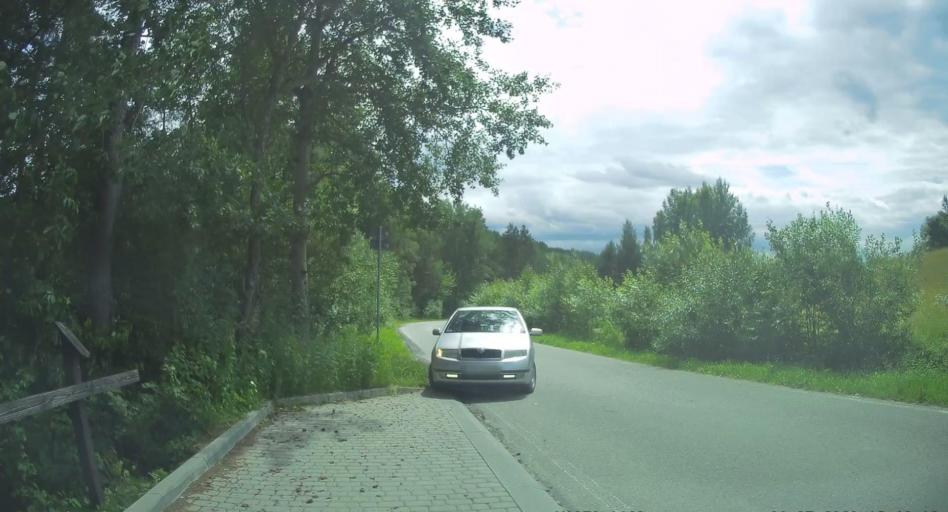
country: PL
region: Lesser Poland Voivodeship
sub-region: Powiat nowosadecki
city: Muszyna
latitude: 49.3877
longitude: 20.9026
